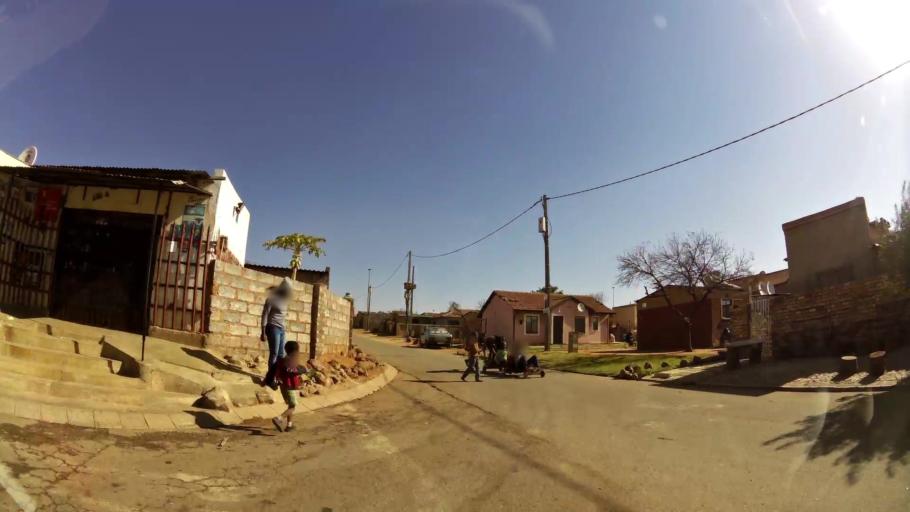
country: ZA
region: Gauteng
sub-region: Ekurhuleni Metropolitan Municipality
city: Tembisa
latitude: -26.0224
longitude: 28.2419
